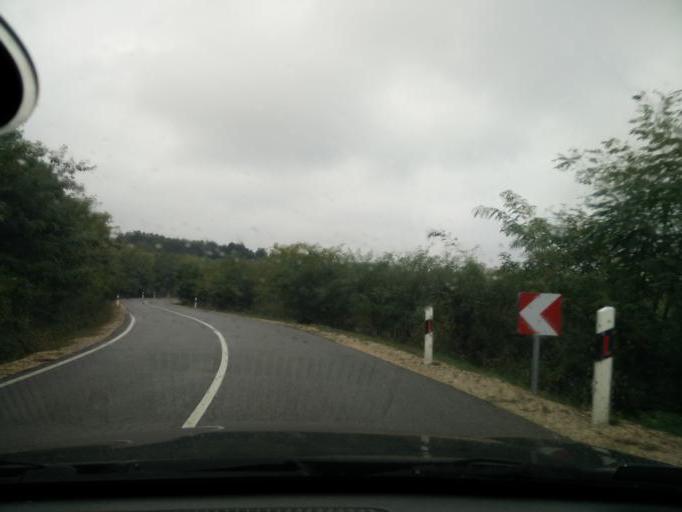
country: HU
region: Komarom-Esztergom
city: Bajna
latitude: 47.6351
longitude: 18.5562
